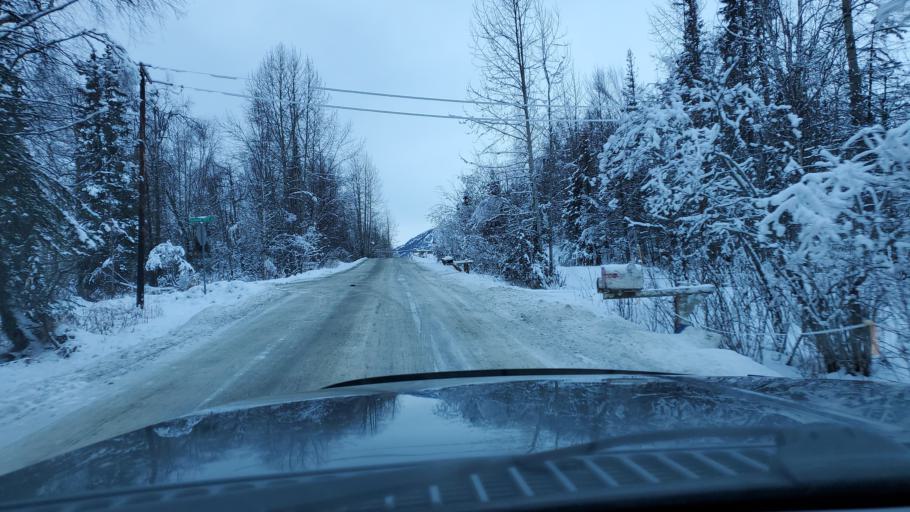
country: US
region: Alaska
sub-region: Matanuska-Susitna Borough
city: Lakes
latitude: 61.6933
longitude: -149.3107
